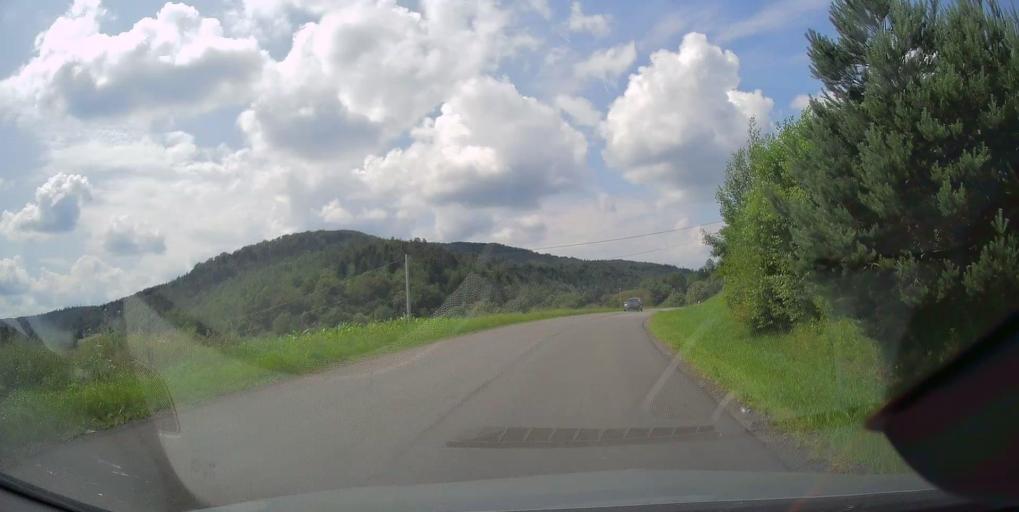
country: PL
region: Lesser Poland Voivodeship
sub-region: Powiat tarnowski
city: Zakliczyn
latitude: 49.7880
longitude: 20.7951
